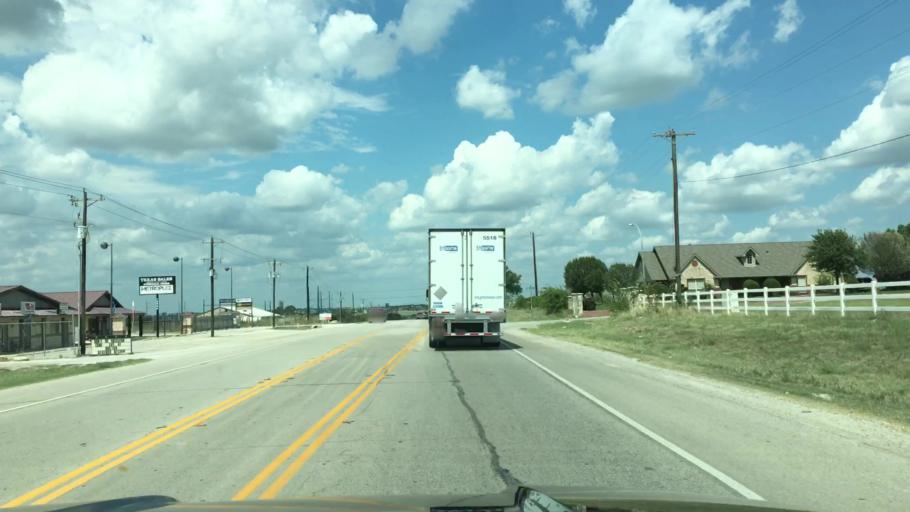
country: US
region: Texas
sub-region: Tarrant County
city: Pecan Acres
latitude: 32.9560
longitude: -97.4208
